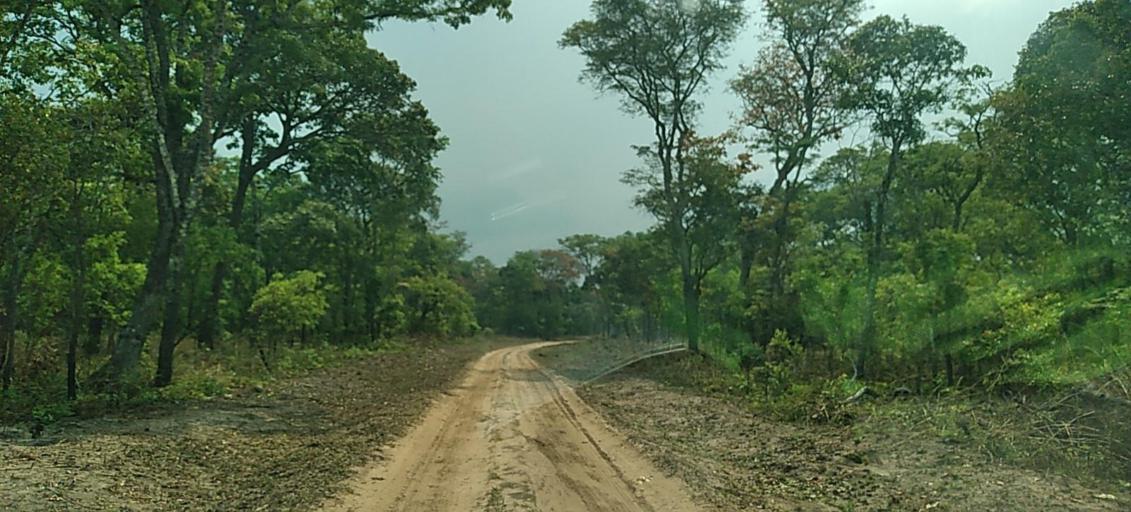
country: ZM
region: North-Western
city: Mwinilunga
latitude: -11.4699
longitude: 24.4884
